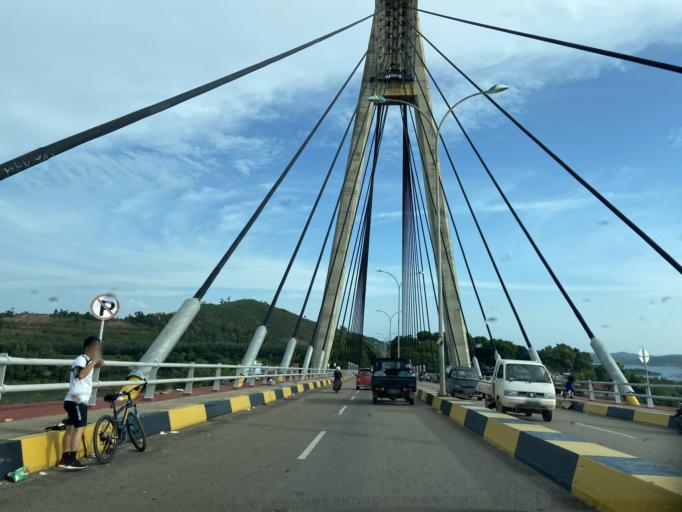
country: SG
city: Singapore
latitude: 0.9819
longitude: 104.0410
